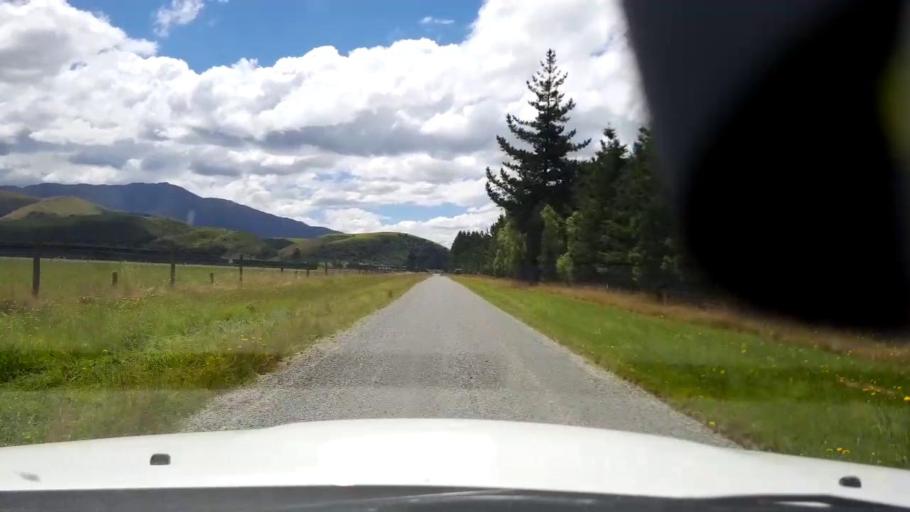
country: NZ
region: Canterbury
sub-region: Timaru District
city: Pleasant Point
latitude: -43.9654
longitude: 171.2268
